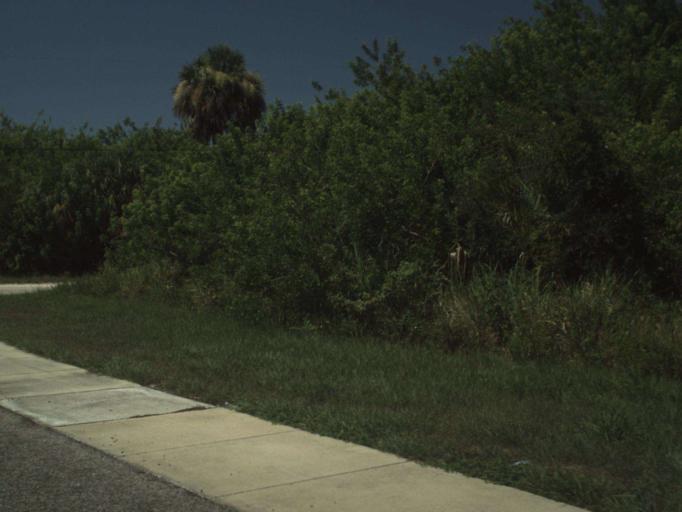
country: US
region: Florida
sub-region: Indian River County
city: Gifford
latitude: 27.6690
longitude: -80.4060
